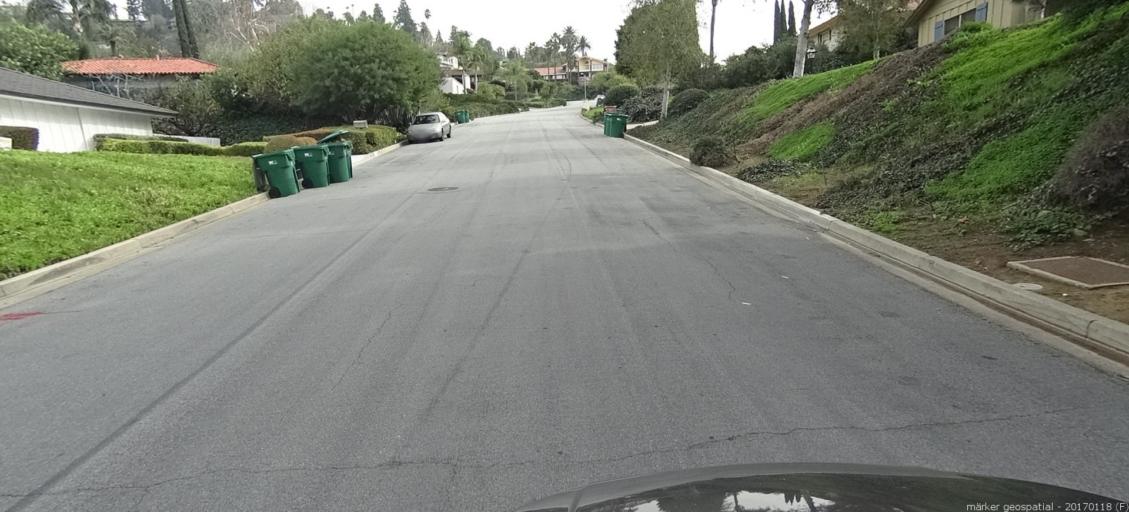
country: US
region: California
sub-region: Orange County
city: North Tustin
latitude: 33.7639
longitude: -117.7887
